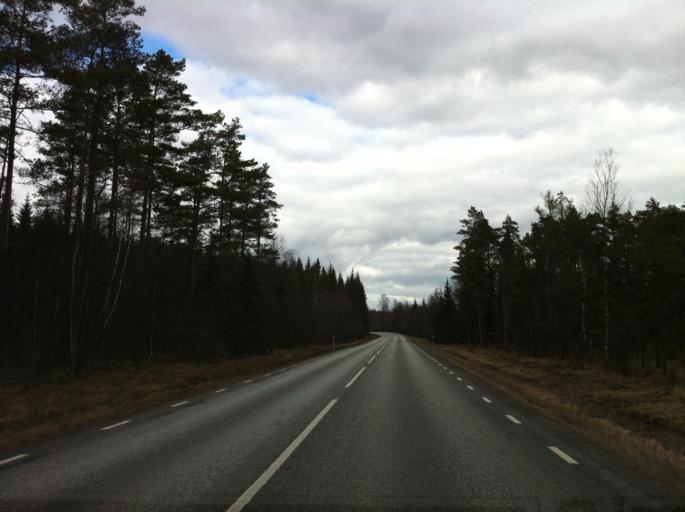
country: SE
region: Vaestra Goetaland
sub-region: Tranemo Kommun
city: Limmared
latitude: 57.5569
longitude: 13.4033
